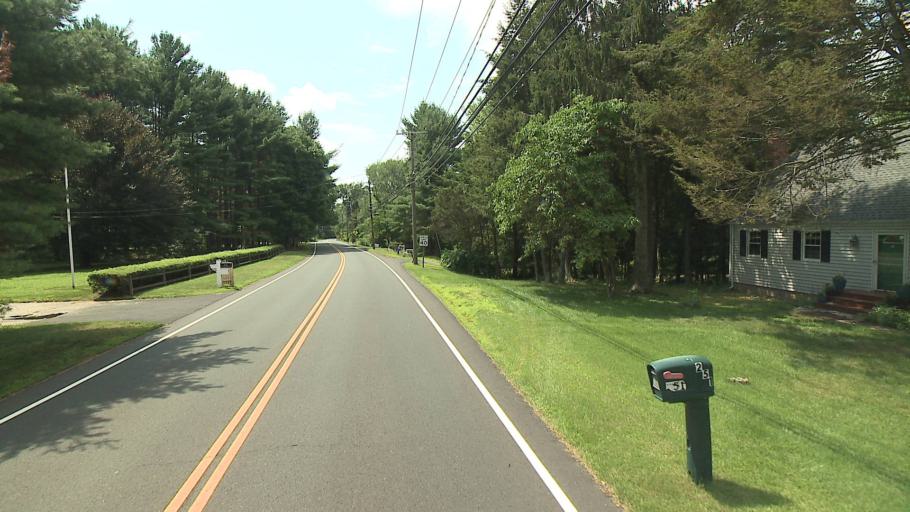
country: US
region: Connecticut
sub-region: Hartford County
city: Collinsville
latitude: 41.7975
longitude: -72.8905
